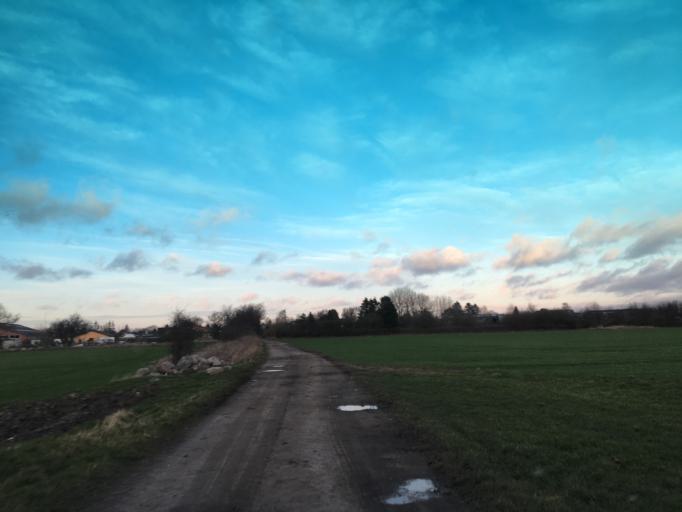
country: DK
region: Capital Region
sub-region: Dragor Kommune
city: Dragor
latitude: 55.5906
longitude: 12.6283
